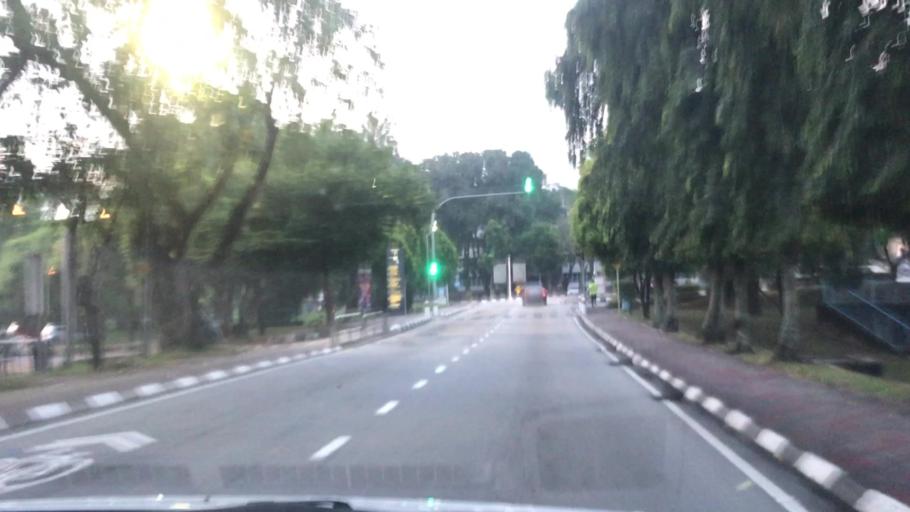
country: MY
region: Kuala Lumpur
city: Kuala Lumpur
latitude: 3.1204
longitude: 101.6546
